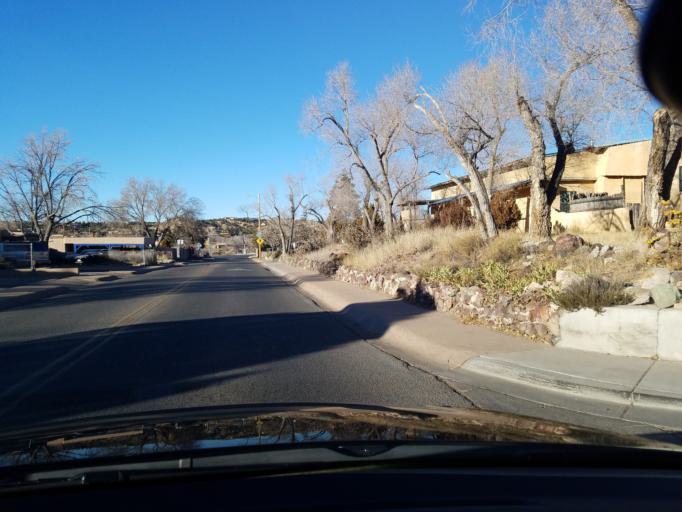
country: US
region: New Mexico
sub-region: Santa Fe County
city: Agua Fria
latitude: 35.6706
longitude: -105.9809
